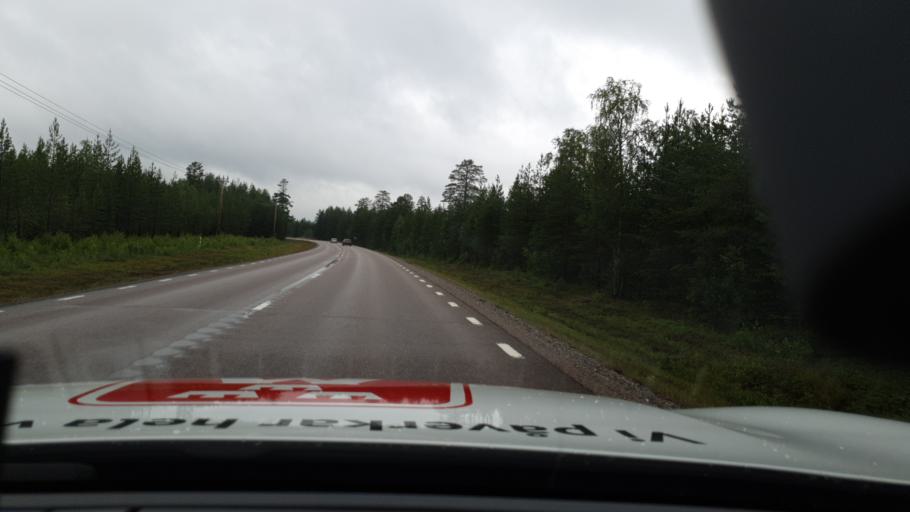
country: SE
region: Norrbotten
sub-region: Kalix Kommun
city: Toere
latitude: 66.0438
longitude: 22.7188
